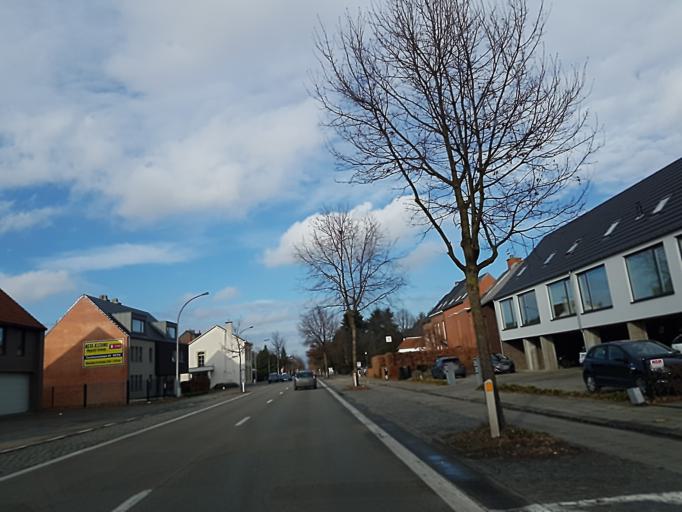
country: BE
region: Flanders
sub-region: Provincie Antwerpen
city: Mol
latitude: 51.1968
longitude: 5.1156
